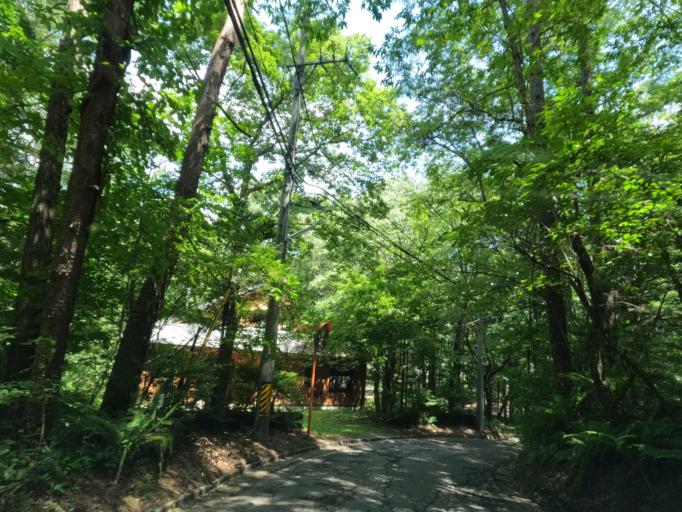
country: JP
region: Nagano
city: Komoro
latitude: 36.3644
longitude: 138.6037
